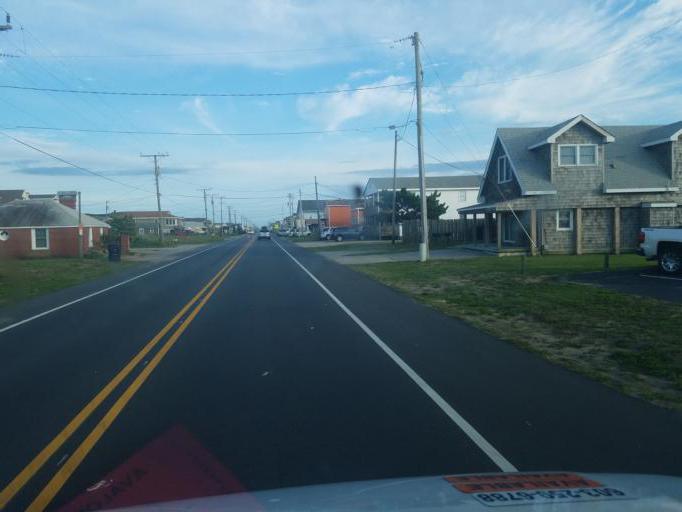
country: US
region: North Carolina
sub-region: Dare County
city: Kill Devil Hills
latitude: 36.0045
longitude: -75.6516
